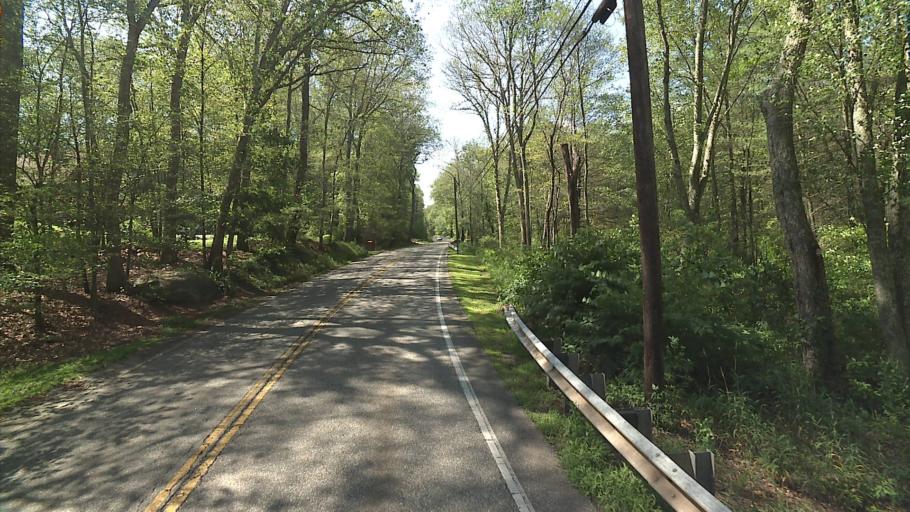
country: US
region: Connecticut
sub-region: Tolland County
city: Mansfield City
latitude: 41.8059
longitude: -72.1709
